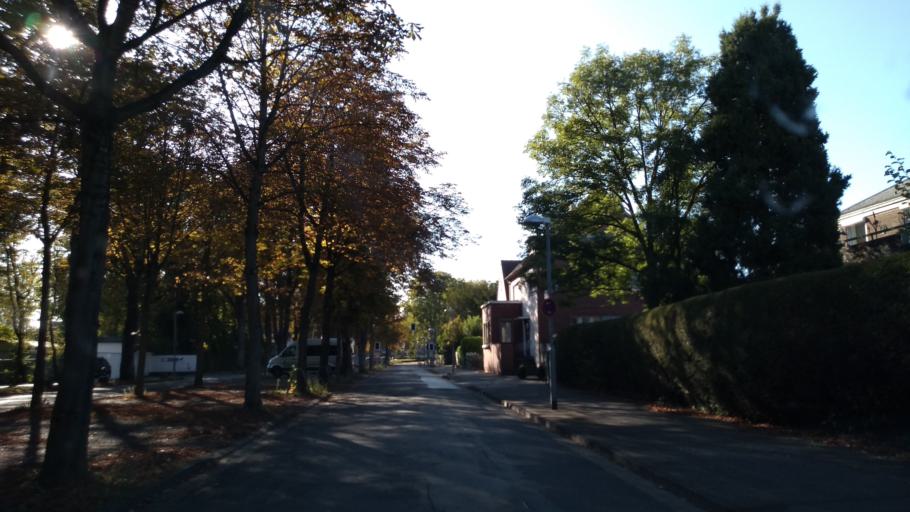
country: DE
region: North Rhine-Westphalia
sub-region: Regierungsbezirk Dusseldorf
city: Dinslaken
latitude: 51.5581
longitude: 6.7350
